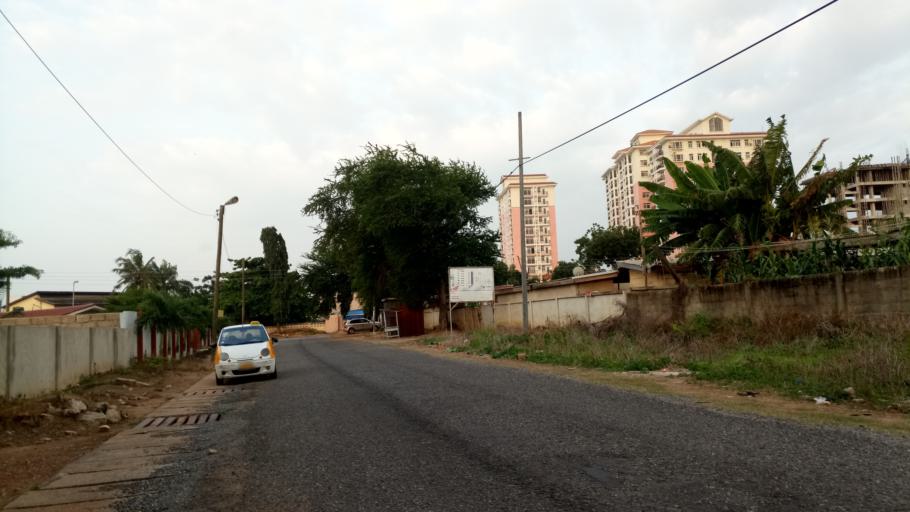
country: GH
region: Greater Accra
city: Accra
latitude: 5.5624
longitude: -0.1883
